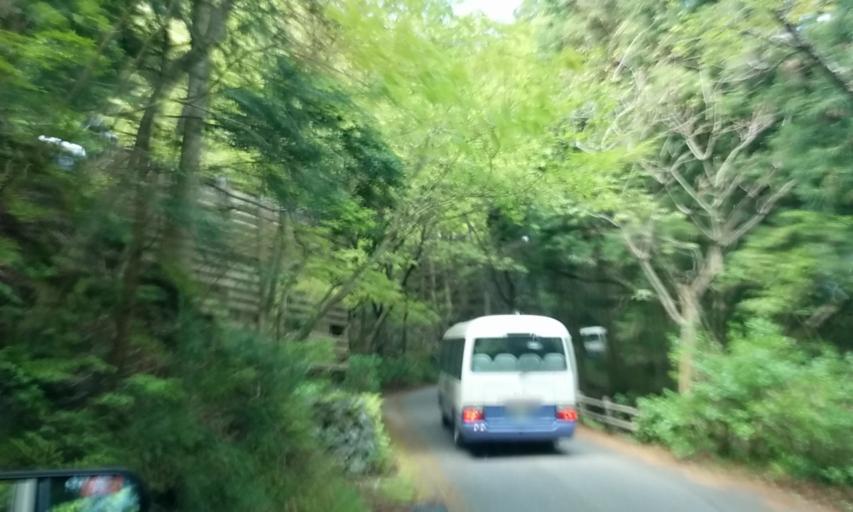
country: JP
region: Ehime
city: Niihama
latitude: 33.8769
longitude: 133.3130
